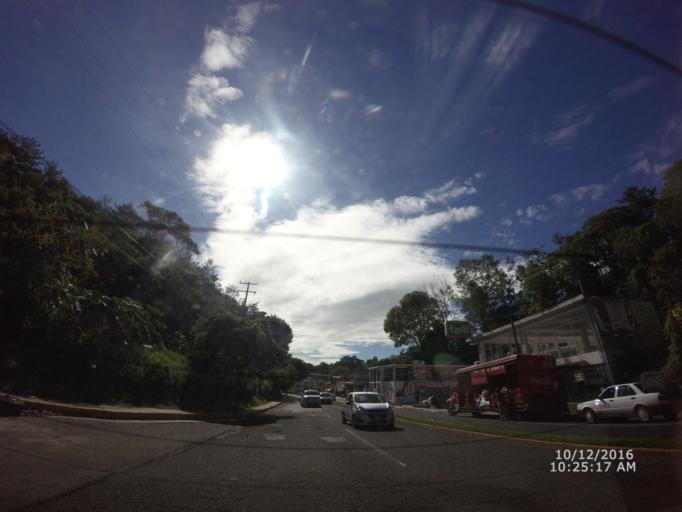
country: TR
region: Sivas
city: Karayun
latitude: 39.6709
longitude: 37.2619
